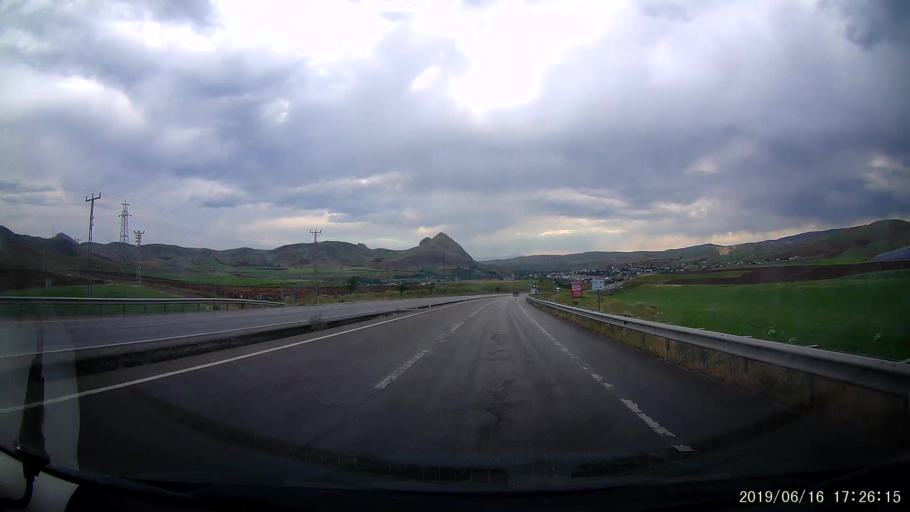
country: TR
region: Erzincan
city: Tercan
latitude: 39.7667
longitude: 40.4167
